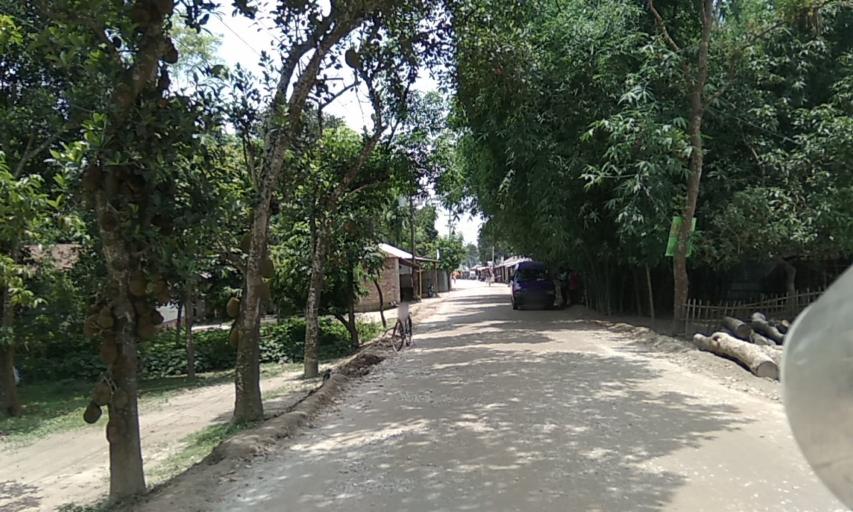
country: BD
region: Rangpur Division
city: Rangpur
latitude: 25.8875
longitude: 89.1854
